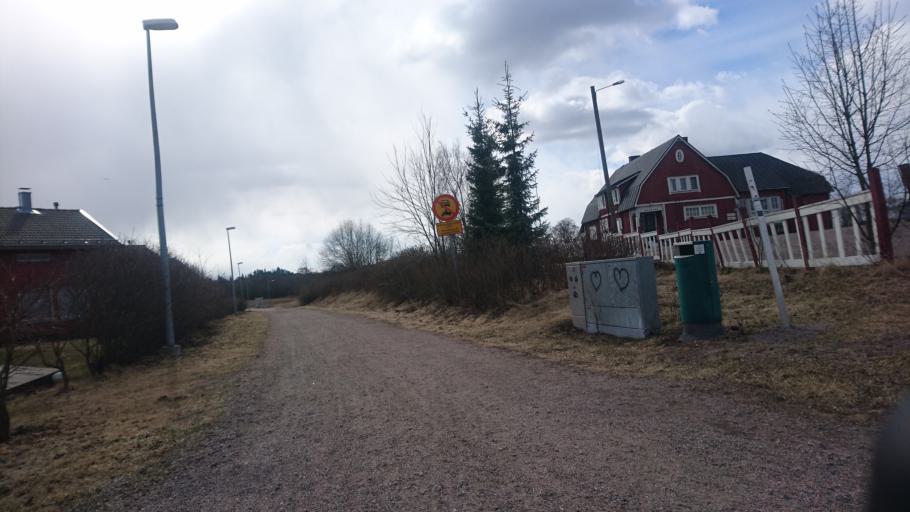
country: FI
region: Uusimaa
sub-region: Helsinki
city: Espoo
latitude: 60.2190
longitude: 24.6699
